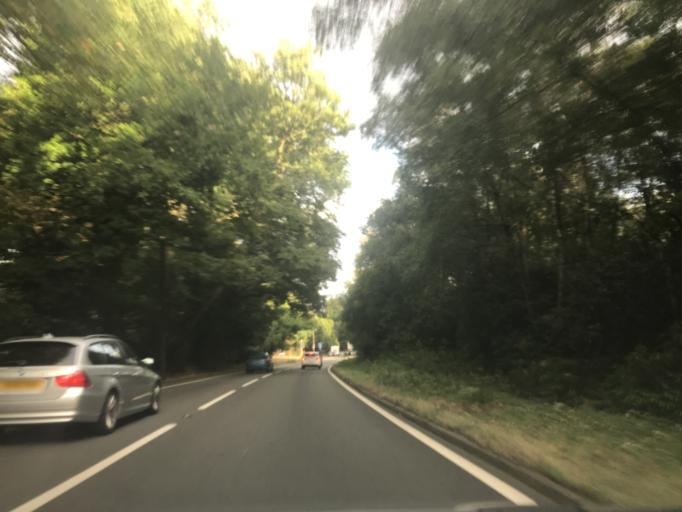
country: GB
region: England
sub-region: Surrey
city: Bagshot
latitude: 51.3738
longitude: -0.6939
